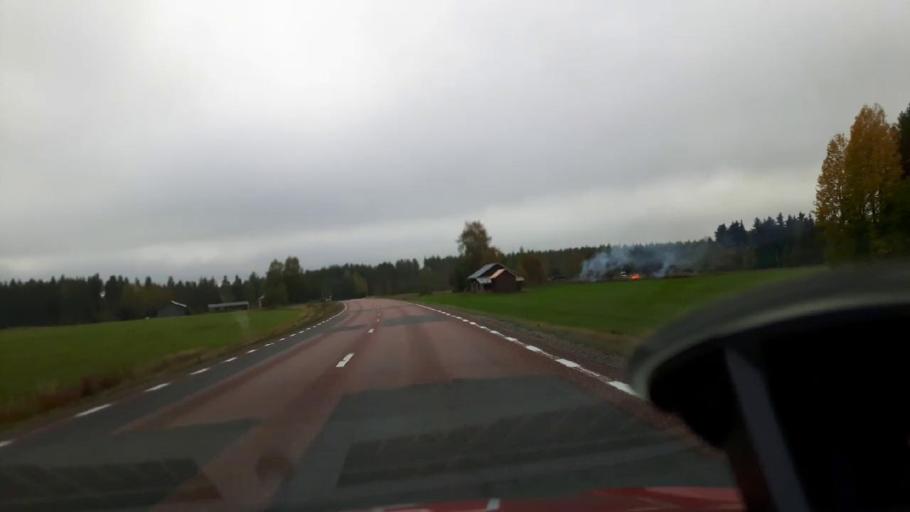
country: SE
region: Gaevleborg
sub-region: Ljusdals Kommun
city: Farila
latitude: 61.8420
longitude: 15.7506
